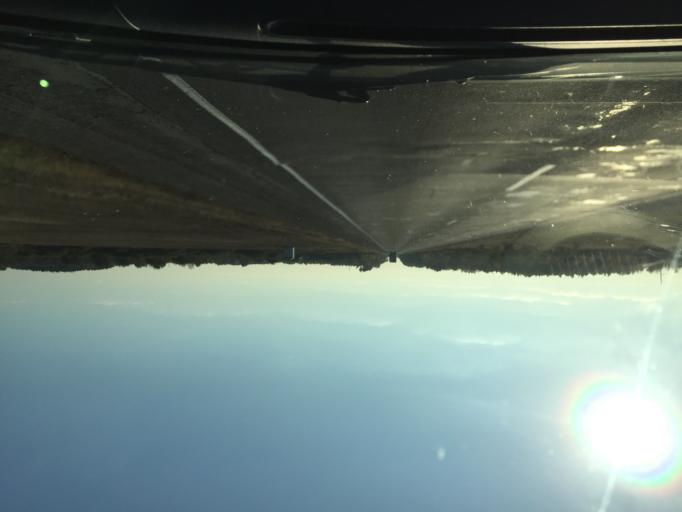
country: BY
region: Brest
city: Horad Luninyets
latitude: 52.3080
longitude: 26.5153
